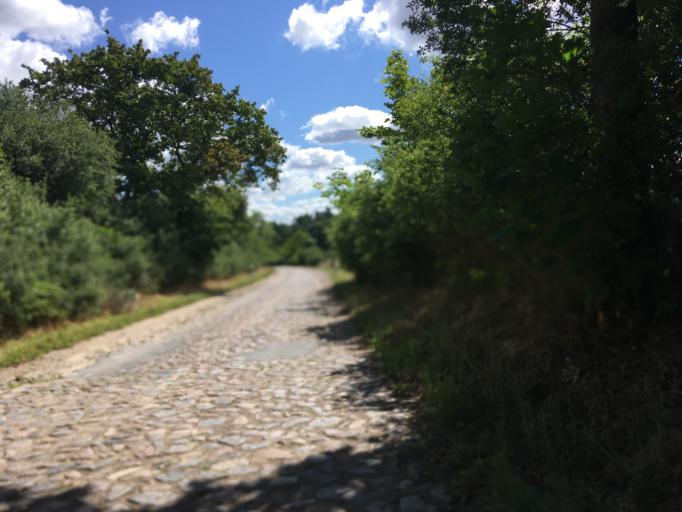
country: DE
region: Brandenburg
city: Mittenwalde
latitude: 53.1944
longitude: 13.6116
